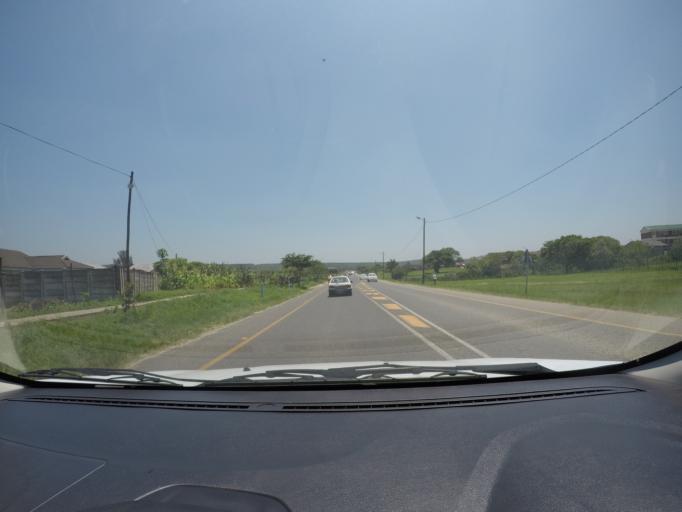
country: ZA
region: KwaZulu-Natal
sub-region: uThungulu District Municipality
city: eSikhawini
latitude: -28.8784
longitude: 31.9023
